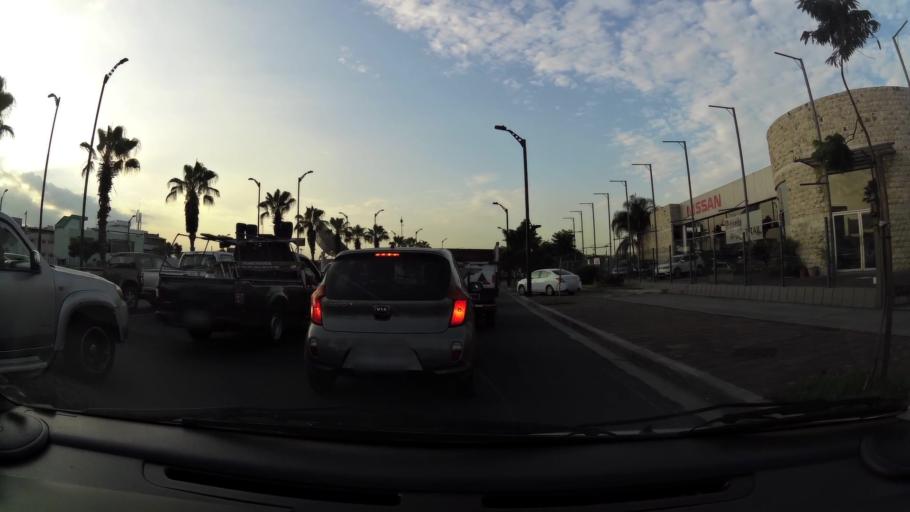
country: EC
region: Guayas
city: Eloy Alfaro
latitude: -2.1485
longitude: -79.8862
